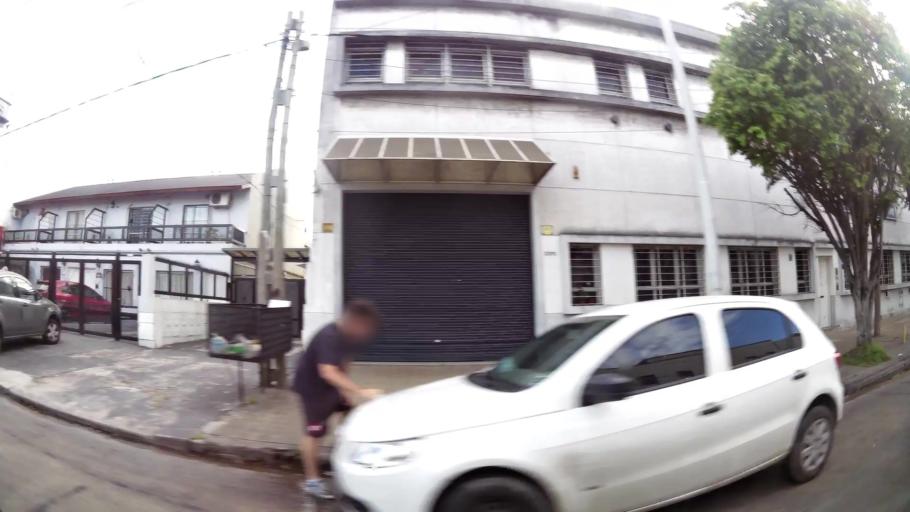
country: AR
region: Buenos Aires
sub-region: Partido de Avellaneda
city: Avellaneda
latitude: -34.6760
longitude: -58.3569
